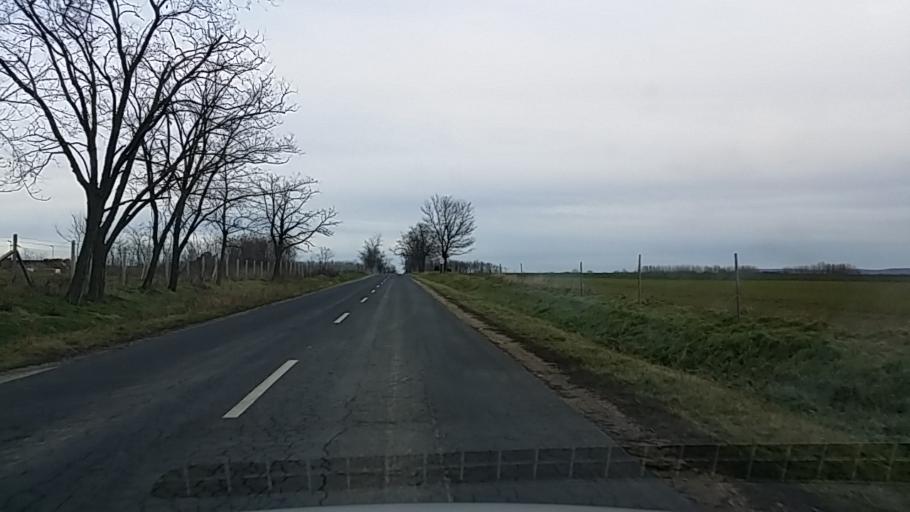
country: HU
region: Veszprem
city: Papa
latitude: 47.3655
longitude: 17.6181
